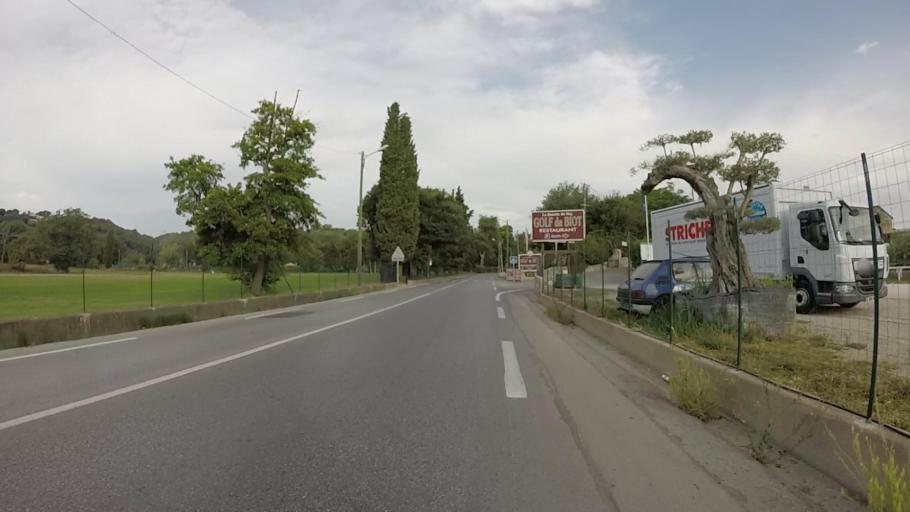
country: FR
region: Provence-Alpes-Cote d'Azur
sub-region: Departement des Alpes-Maritimes
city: Biot
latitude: 43.6168
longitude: 7.1054
